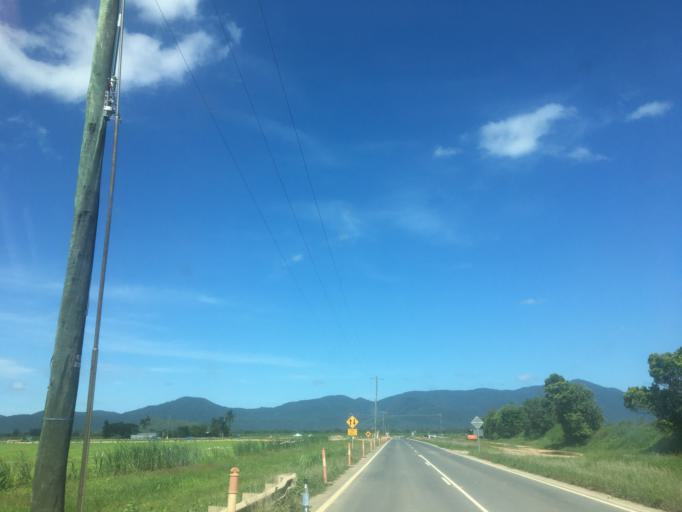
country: AU
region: Queensland
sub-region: Cairns
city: Woree
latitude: -17.0603
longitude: 145.7664
